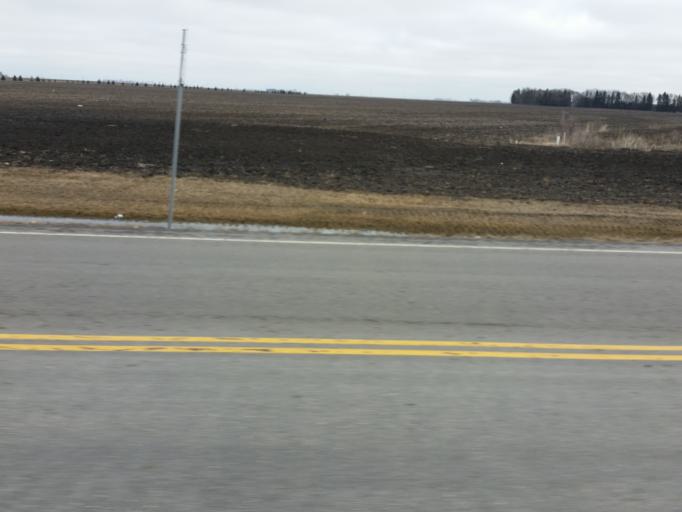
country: US
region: North Dakota
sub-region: Cass County
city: Casselton
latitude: 46.9066
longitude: -97.2198
